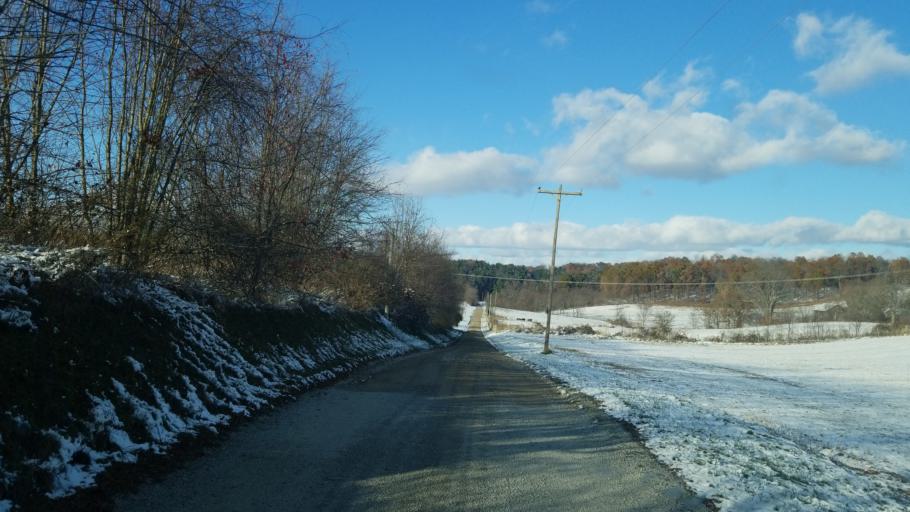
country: US
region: Ohio
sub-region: Licking County
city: Newark
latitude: 40.1472
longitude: -82.3888
